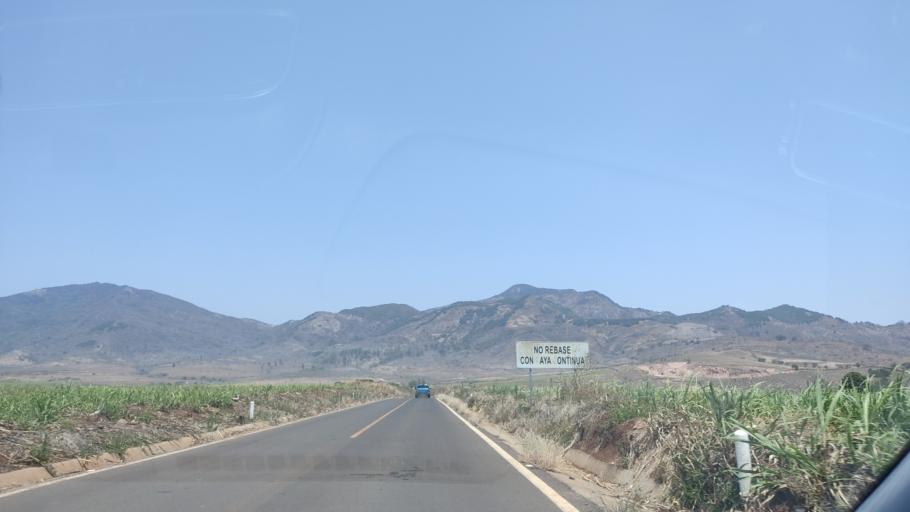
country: MX
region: Nayarit
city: Puga
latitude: 21.6026
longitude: -104.7390
